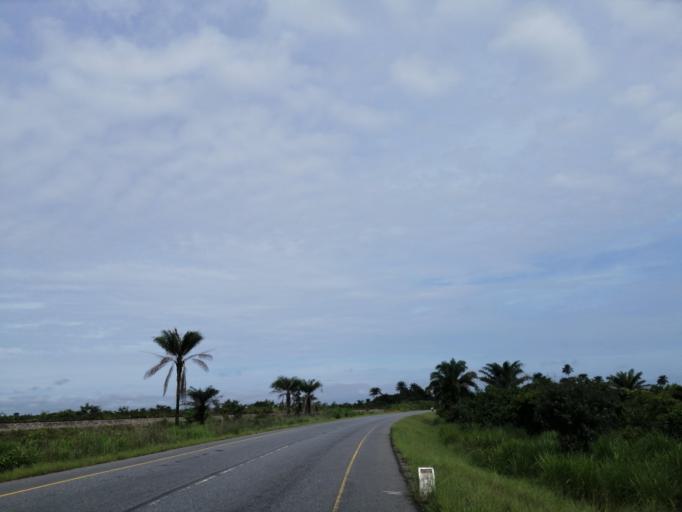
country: SL
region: Northern Province
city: Port Loko
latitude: 8.7696
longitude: -12.8737
